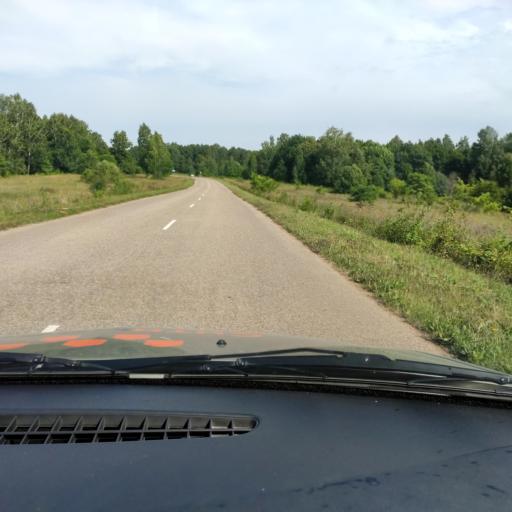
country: RU
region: Bashkortostan
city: Pavlovka
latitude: 55.3857
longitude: 56.5004
